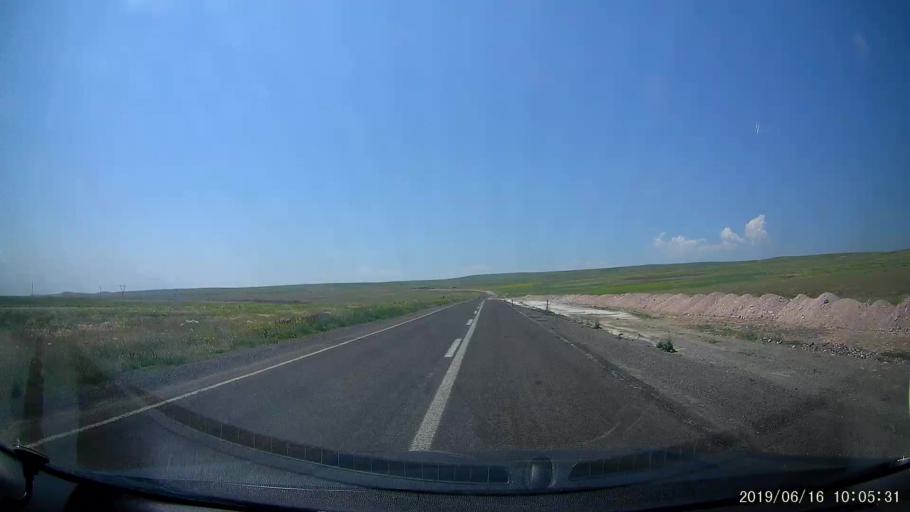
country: TR
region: Kars
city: Digor
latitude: 40.2692
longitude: 43.5385
